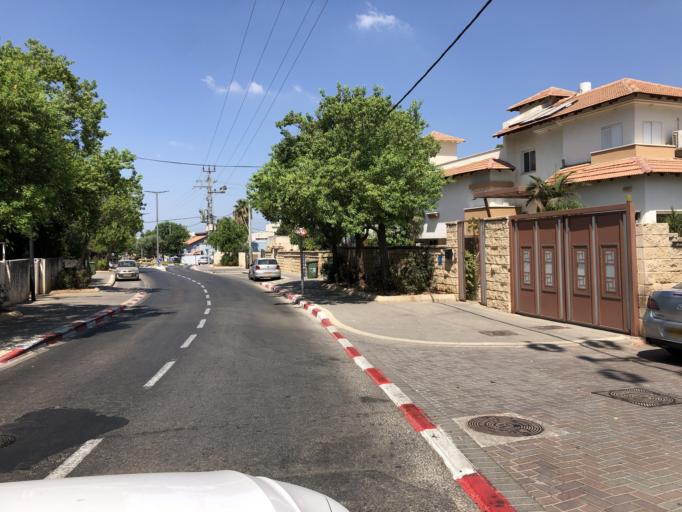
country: IL
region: Central District
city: Rosh Ha'Ayin
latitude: 32.0994
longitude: 34.9559
